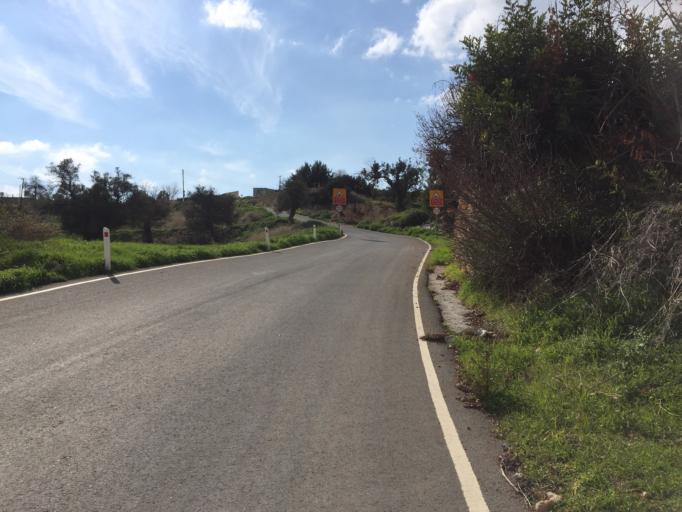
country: CY
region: Larnaka
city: Agios Tychon
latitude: 34.7459
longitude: 33.1315
